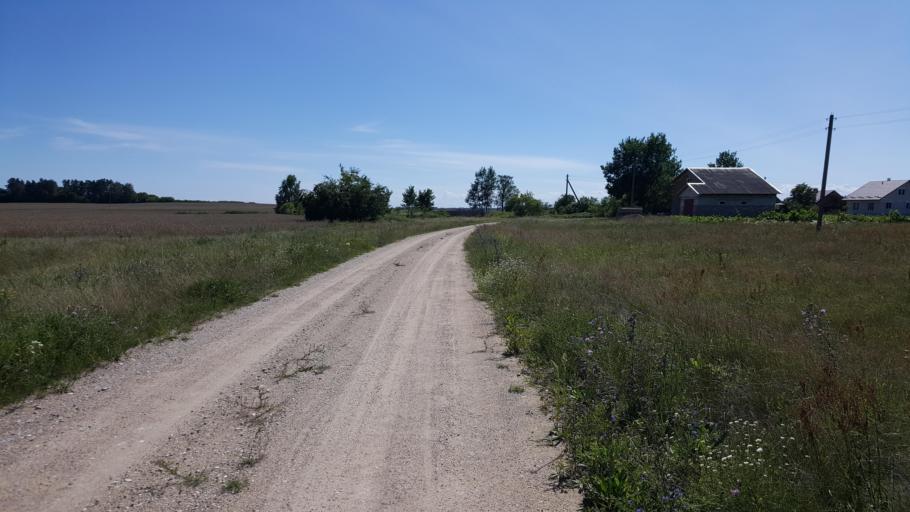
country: BY
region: Brest
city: Charnawchytsy
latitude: 52.2114
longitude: 23.7986
